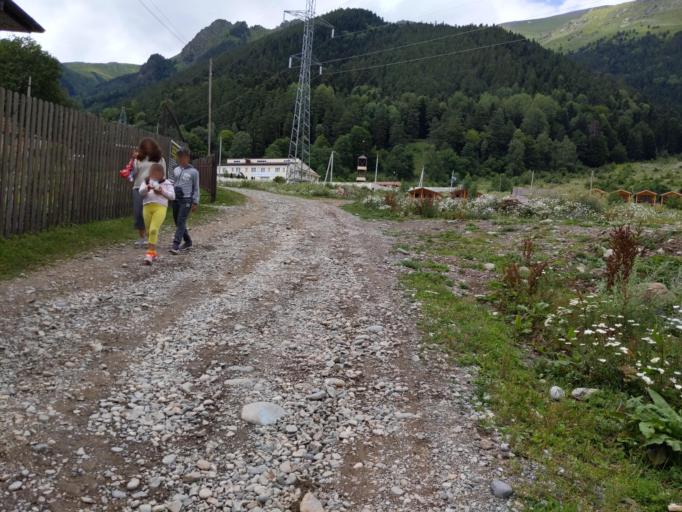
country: RU
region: Karachayevo-Cherkesiya
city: Nizhniy Arkhyz
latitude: 43.5667
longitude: 41.2676
